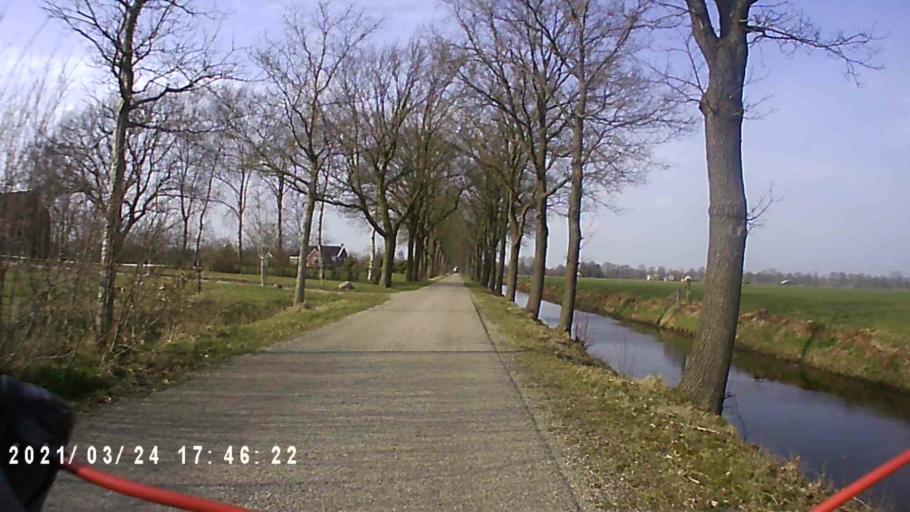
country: NL
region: Groningen
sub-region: Gemeente Leek
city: Leek
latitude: 53.1110
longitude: 6.3368
